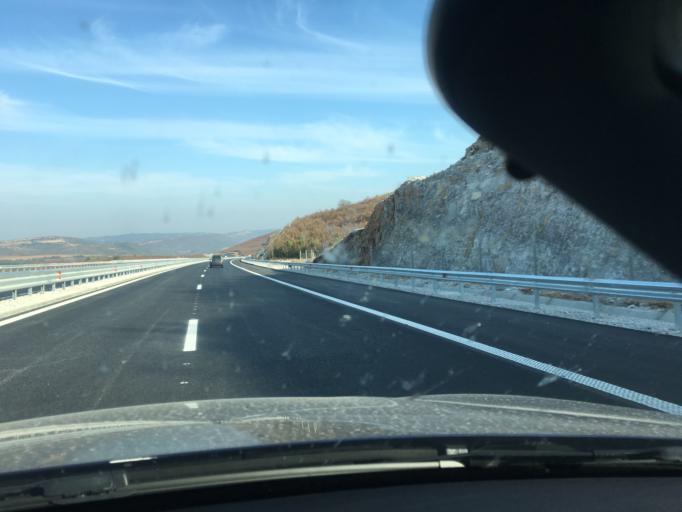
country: BG
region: Lovech
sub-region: Obshtina Yablanitsa
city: Yablanitsa
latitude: 43.0527
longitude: 24.1754
